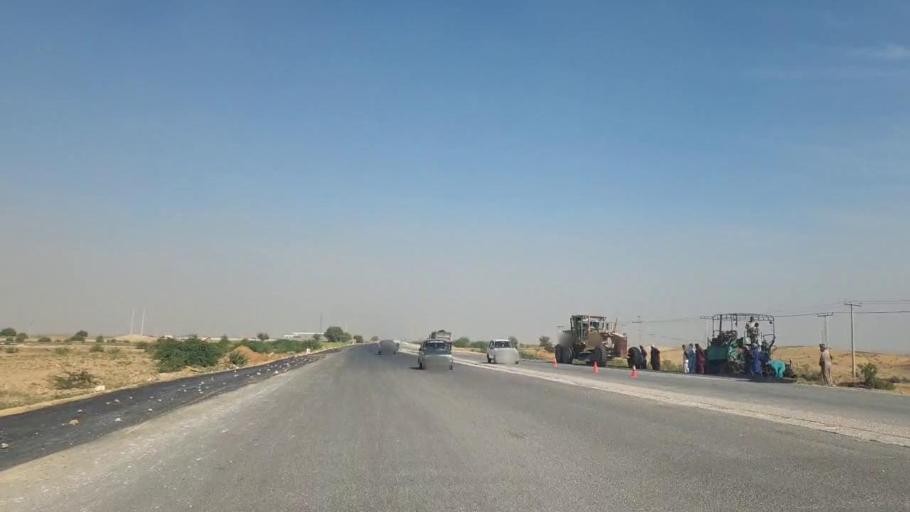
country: PK
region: Sindh
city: Jamshoro
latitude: 25.5301
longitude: 68.2806
